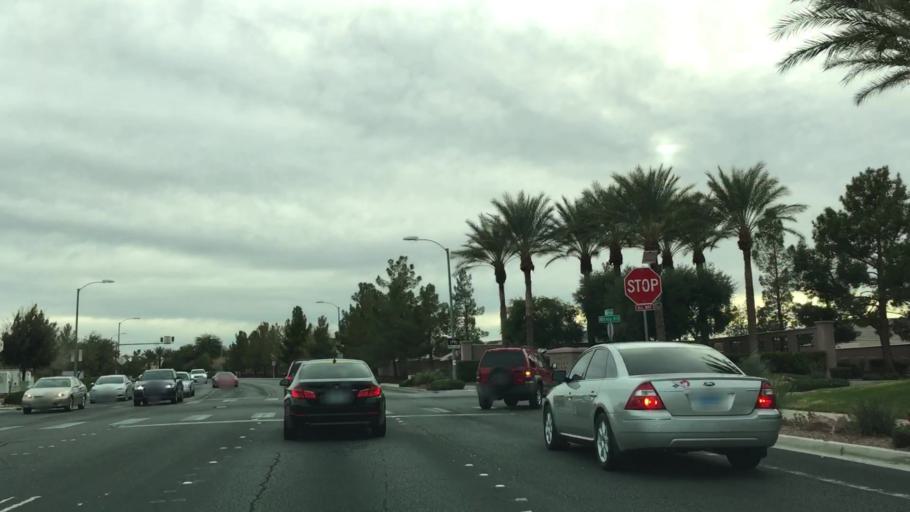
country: US
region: Nevada
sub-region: Clark County
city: Whitney
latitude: 36.0128
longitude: -115.0948
